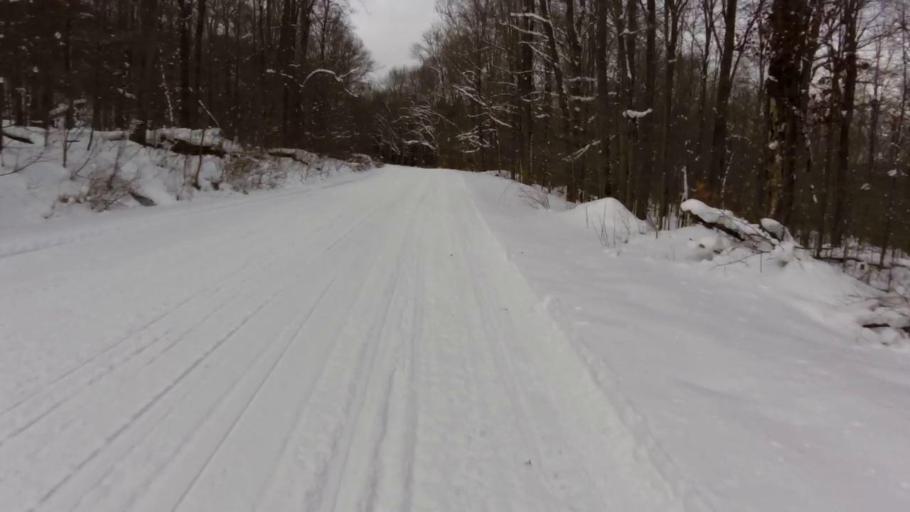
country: US
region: New York
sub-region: Cattaraugus County
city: Salamanca
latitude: 42.0711
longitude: -78.7575
